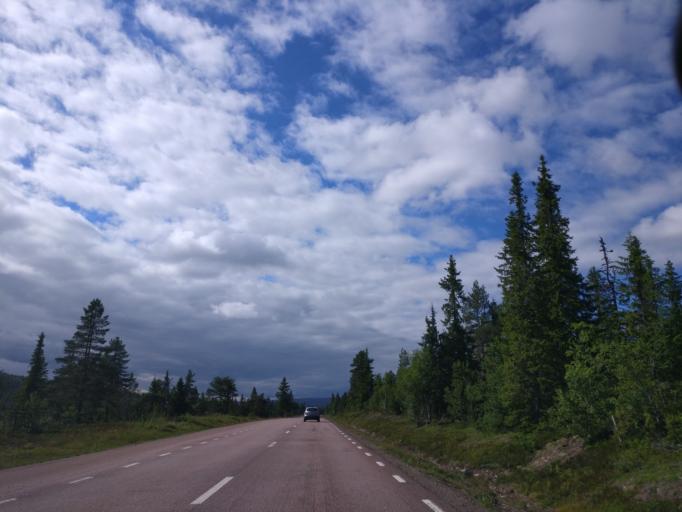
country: SE
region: Dalarna
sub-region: Malung-Saelens kommun
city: Malung
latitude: 61.1663
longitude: 13.0981
